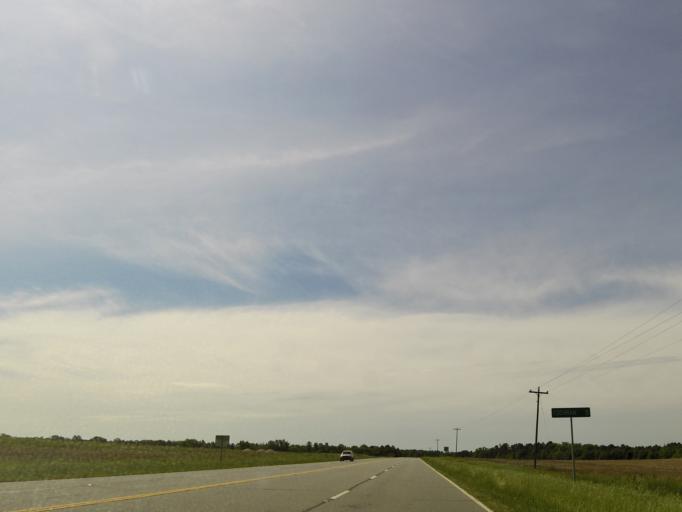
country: US
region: Georgia
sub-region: Bleckley County
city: Cochran
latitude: 32.4450
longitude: -83.3789
